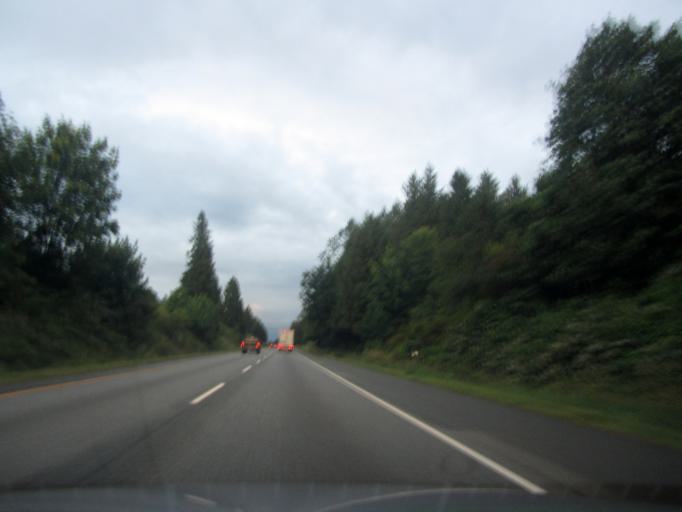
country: CA
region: British Columbia
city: Aldergrove
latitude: 49.0743
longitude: -122.4243
